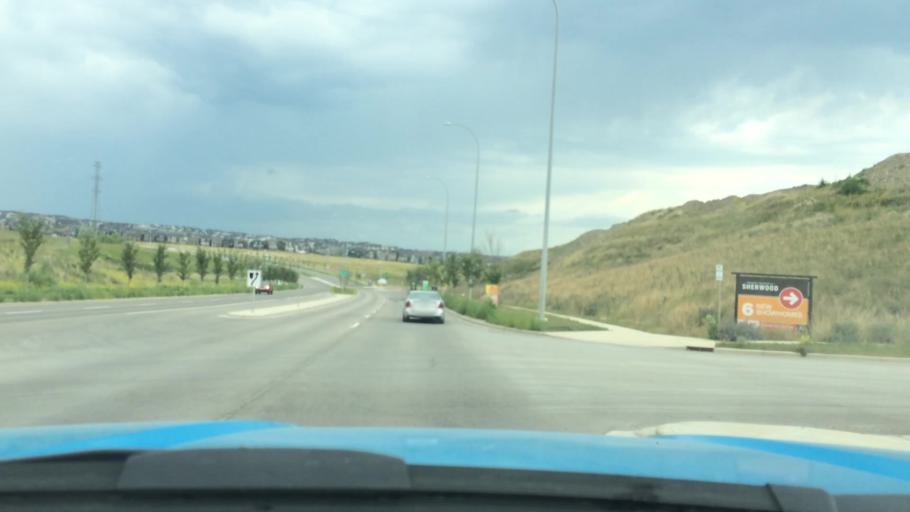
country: CA
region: Alberta
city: Calgary
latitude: 51.1650
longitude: -114.1633
